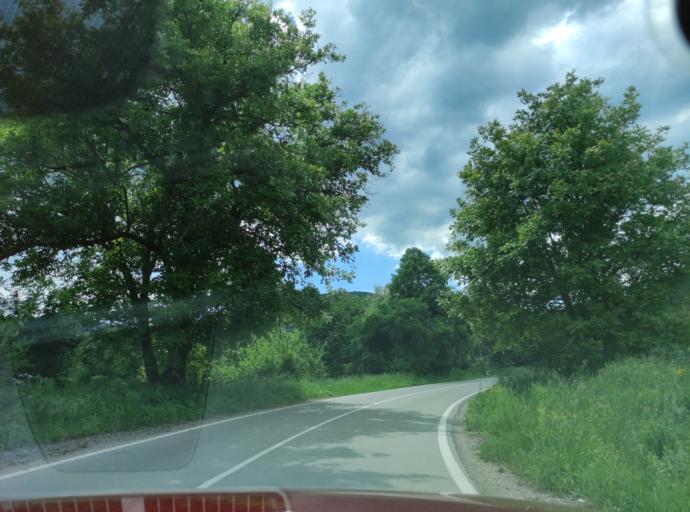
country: BG
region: Montana
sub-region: Obshtina Chiprovtsi
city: Chiprovtsi
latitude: 43.4423
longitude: 22.9313
